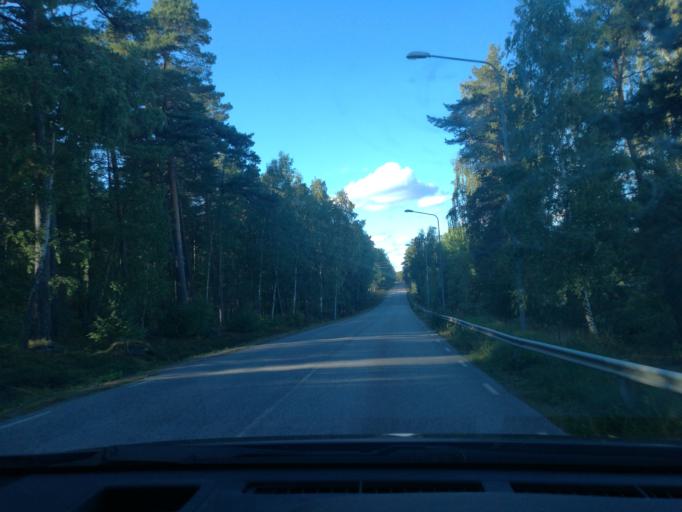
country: SE
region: Vaestmanland
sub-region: Kungsors Kommun
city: Kungsoer
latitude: 59.4130
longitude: 16.1063
